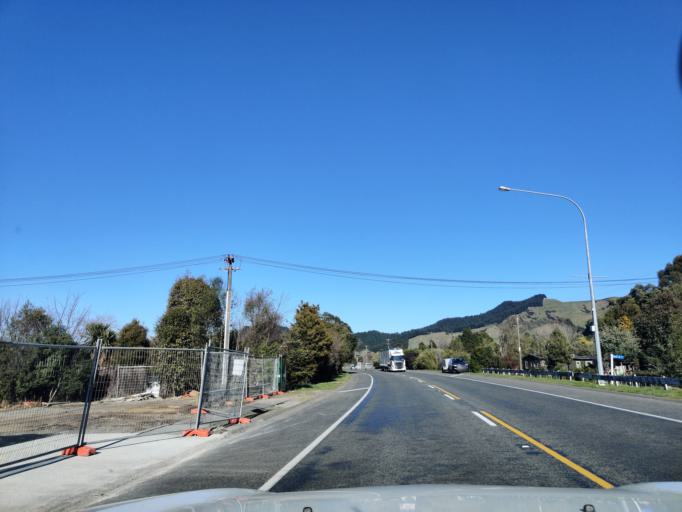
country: NZ
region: Manawatu-Wanganui
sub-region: Ruapehu District
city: Waiouru
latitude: -39.8101
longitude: 175.7872
